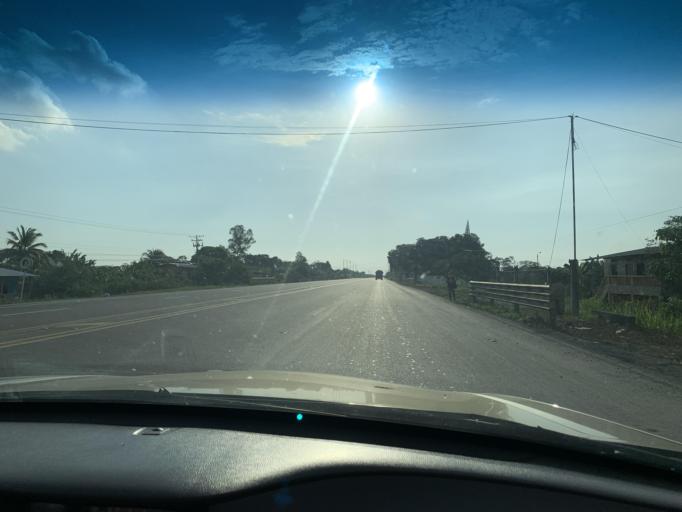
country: EC
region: Guayas
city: Naranjito
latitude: -2.2563
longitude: -79.5934
